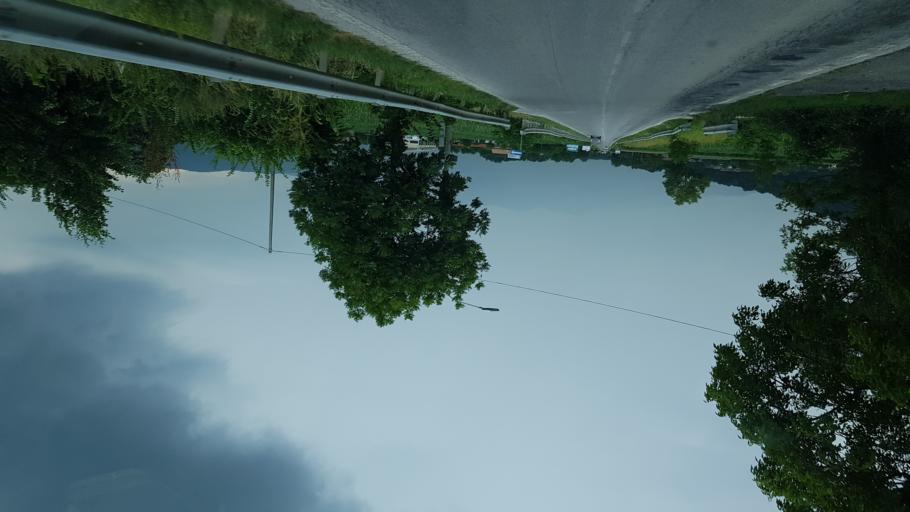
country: IT
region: Piedmont
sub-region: Provincia di Cuneo
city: Caraglio
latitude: 44.4329
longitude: 7.4224
